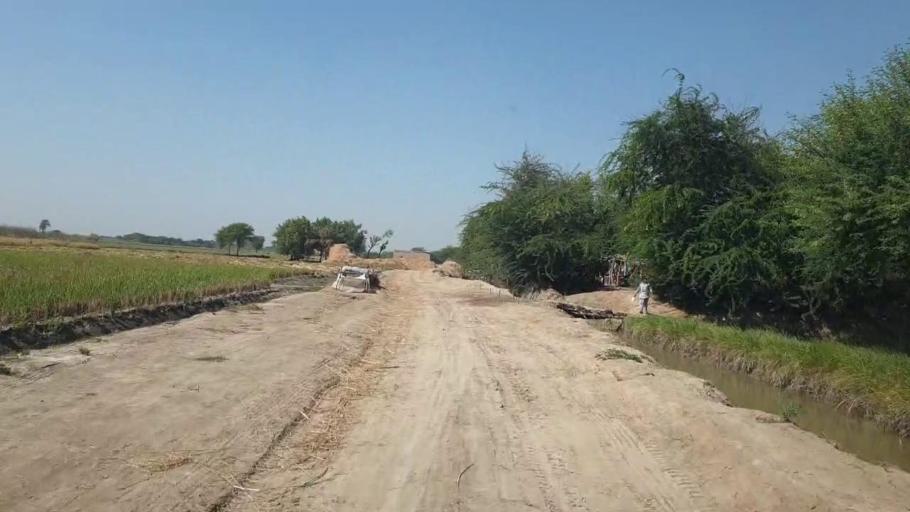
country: PK
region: Sindh
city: Talhar
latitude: 24.8060
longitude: 68.8030
